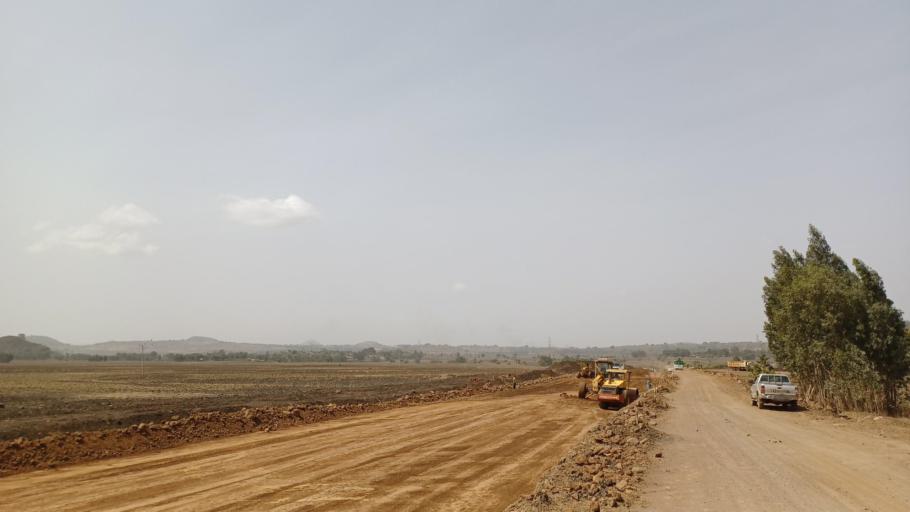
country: ET
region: Amhara
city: Bahir Dar
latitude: 11.8414
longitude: 37.0018
